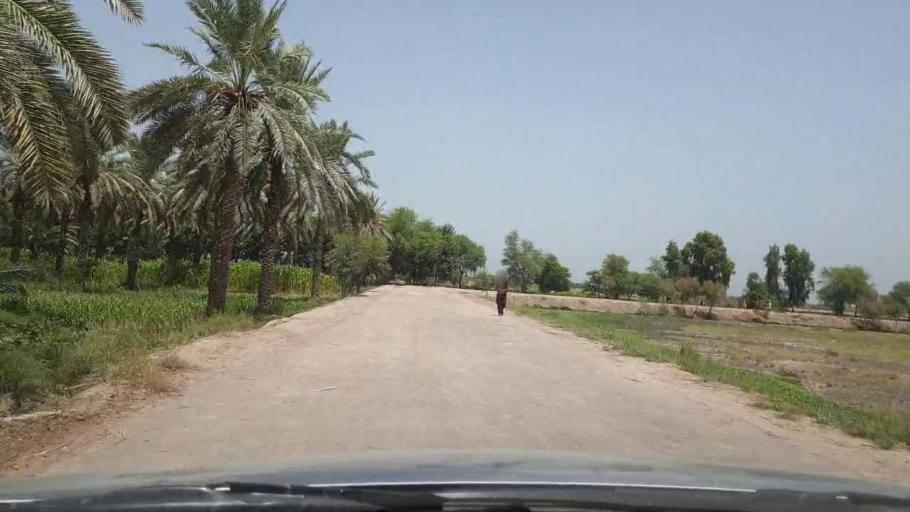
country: PK
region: Sindh
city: Pano Aqil
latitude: 27.8750
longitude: 69.1546
